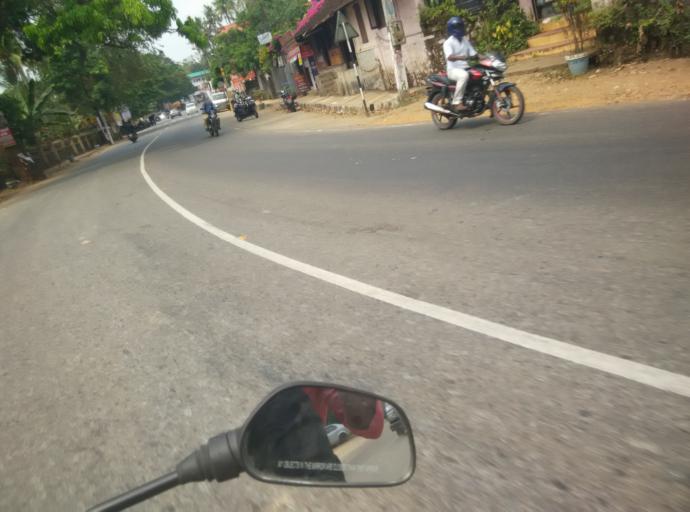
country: IN
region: Kerala
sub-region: Kottayam
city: Lalam
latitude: 9.7023
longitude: 76.6672
